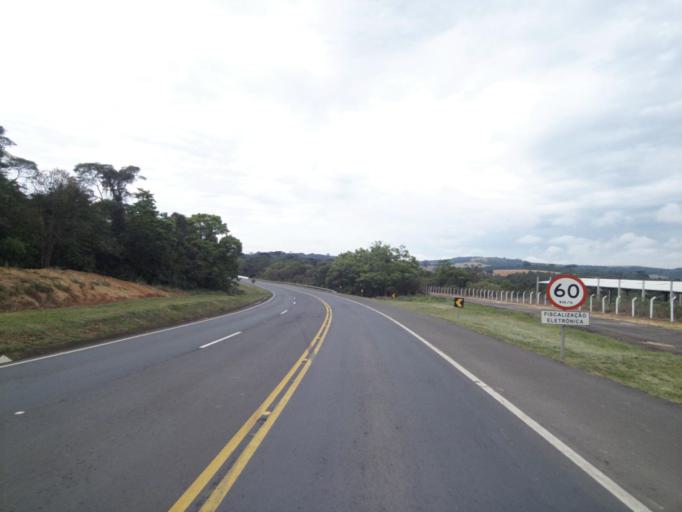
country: BR
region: Parana
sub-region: Irati
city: Irati
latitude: -25.4556
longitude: -50.6275
